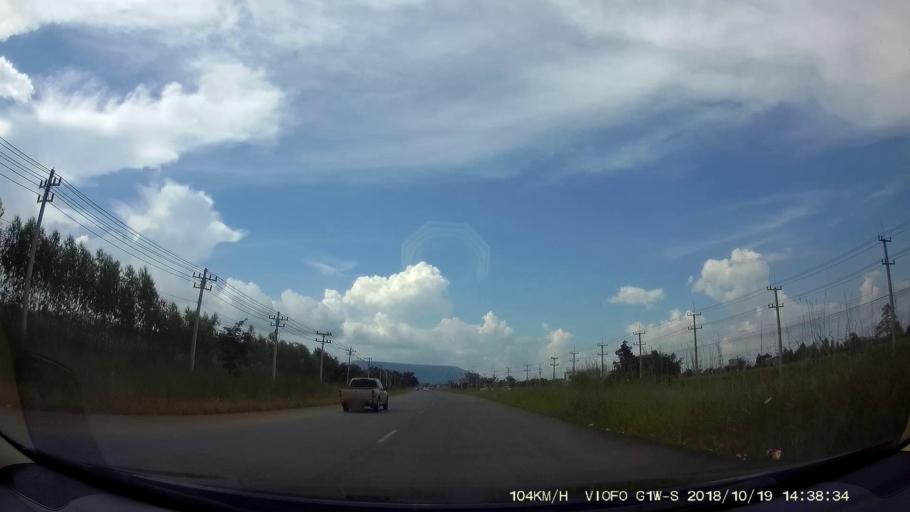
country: TH
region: Chaiyaphum
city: Kaeng Khro
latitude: 16.2150
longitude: 102.2009
